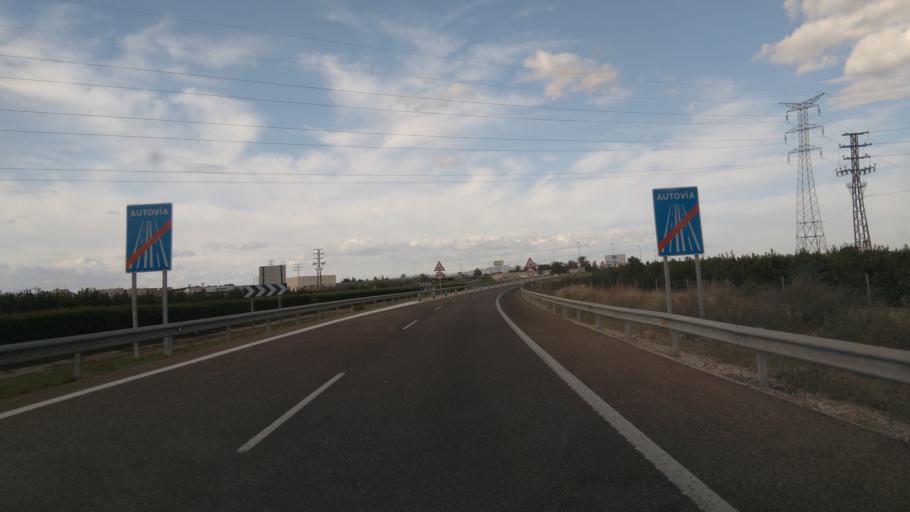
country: ES
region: Valencia
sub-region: Provincia de Valencia
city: L'Alcudia
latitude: 39.1888
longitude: -0.4932
